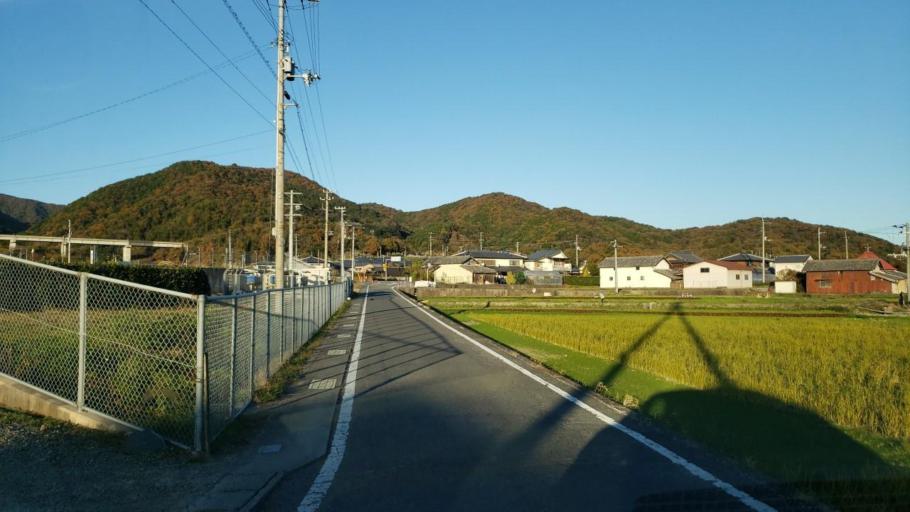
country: JP
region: Tokushima
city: Kamojimacho-jogejima
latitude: 34.0991
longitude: 134.2976
